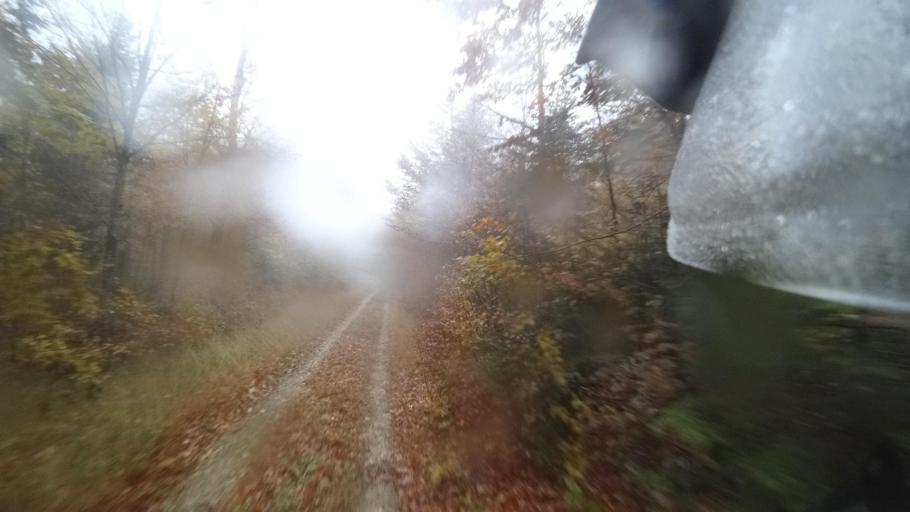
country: HR
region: Primorsko-Goranska
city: Vrbovsko
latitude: 45.2821
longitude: 14.9687
